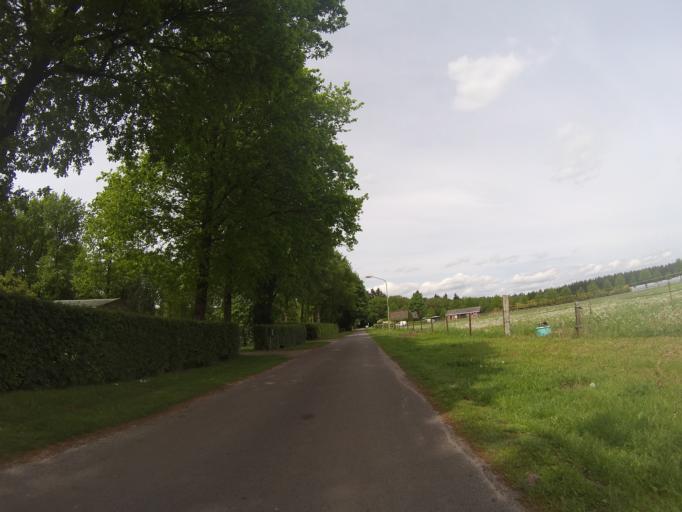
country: NL
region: Drenthe
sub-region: Gemeente Borger-Odoorn
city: Borger
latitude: 52.8602
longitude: 6.7440
